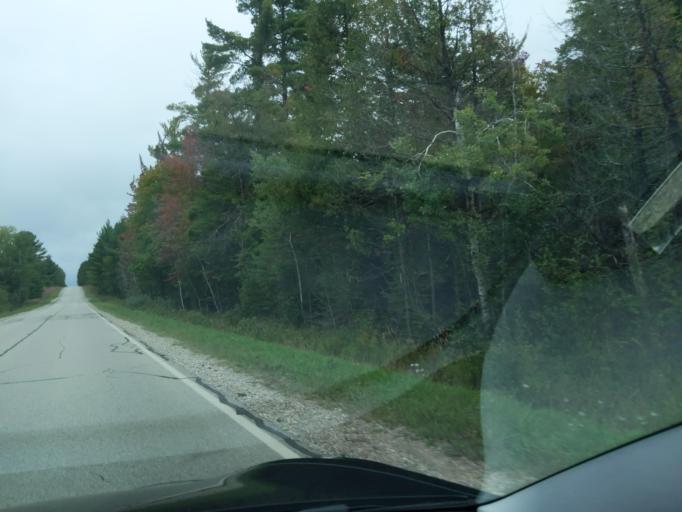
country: US
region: Michigan
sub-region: Grand Traverse County
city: Kingsley
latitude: 44.6183
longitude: -85.3532
